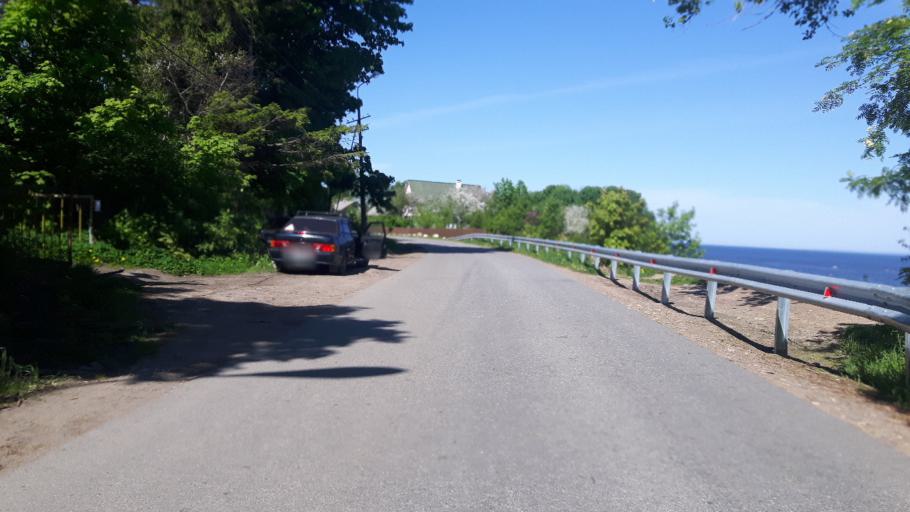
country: RU
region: Leningrad
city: Lebyazh'ye
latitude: 59.9715
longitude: 29.3819
